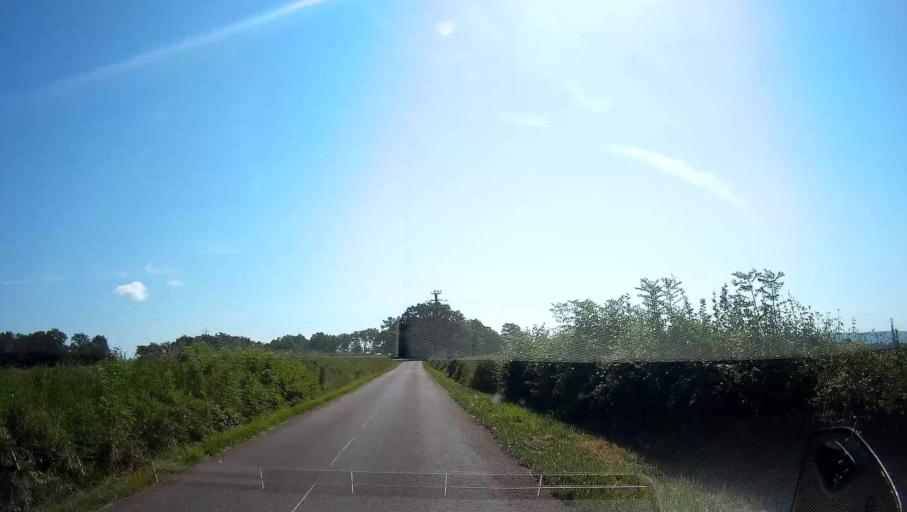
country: FR
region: Bourgogne
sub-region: Departement de Saone-et-Loire
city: Couches
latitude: 46.8842
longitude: 4.5475
